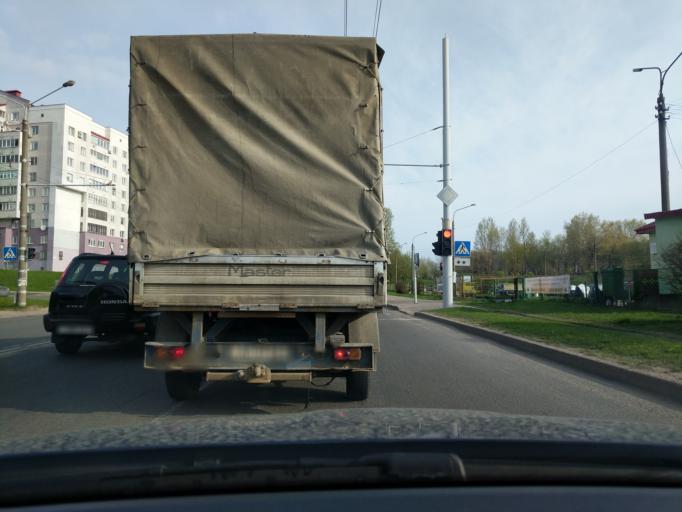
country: BY
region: Minsk
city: Novoye Medvezhino
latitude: 53.9035
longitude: 27.4631
